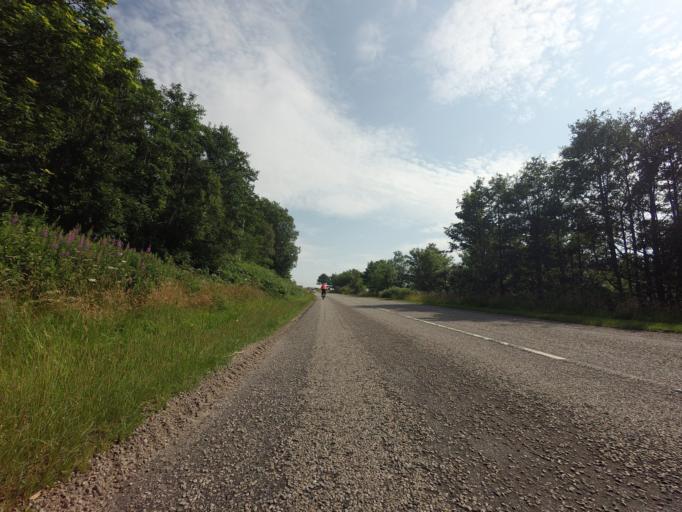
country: GB
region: Scotland
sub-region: Highland
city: Evanton
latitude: 57.9199
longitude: -4.3977
